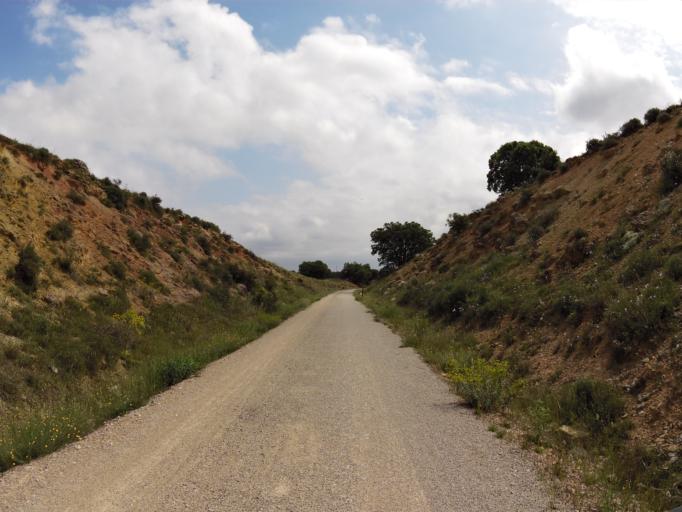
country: ES
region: Castille-La Mancha
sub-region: Provincia de Albacete
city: Robledo
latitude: 38.7739
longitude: -2.4410
